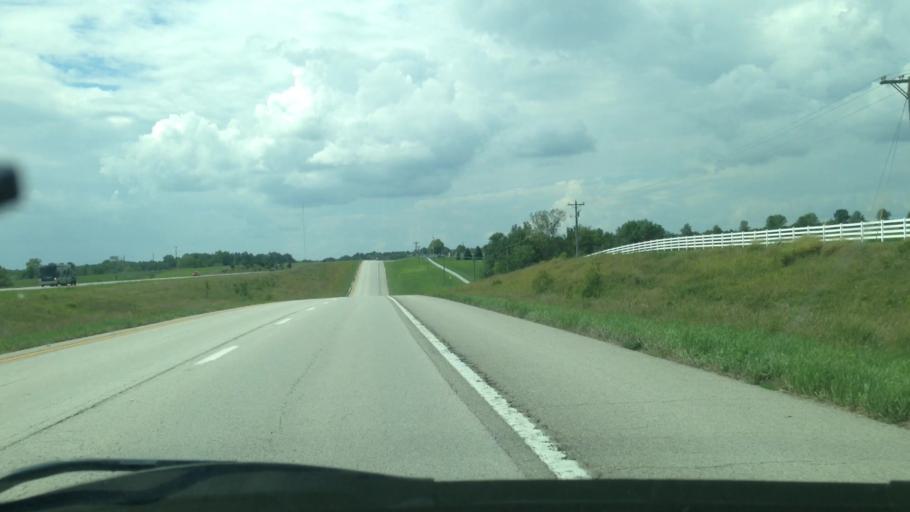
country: US
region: Missouri
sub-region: Pike County
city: Bowling Green
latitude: 39.2536
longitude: -91.0440
